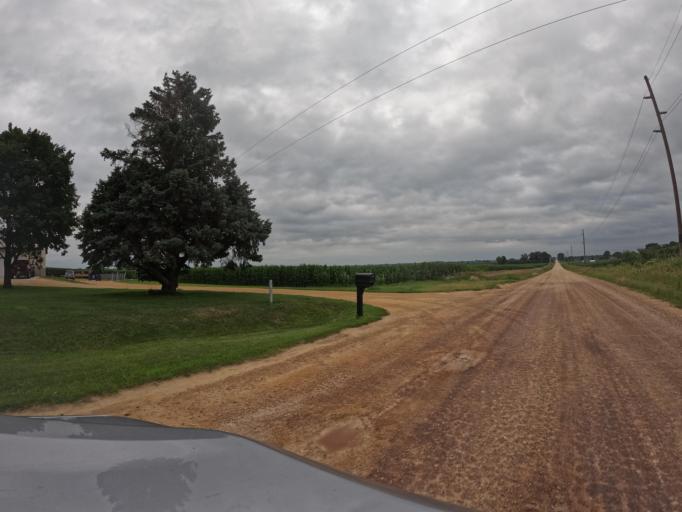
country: US
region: Iowa
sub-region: Clinton County
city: De Witt
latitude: 41.7863
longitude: -90.4572
